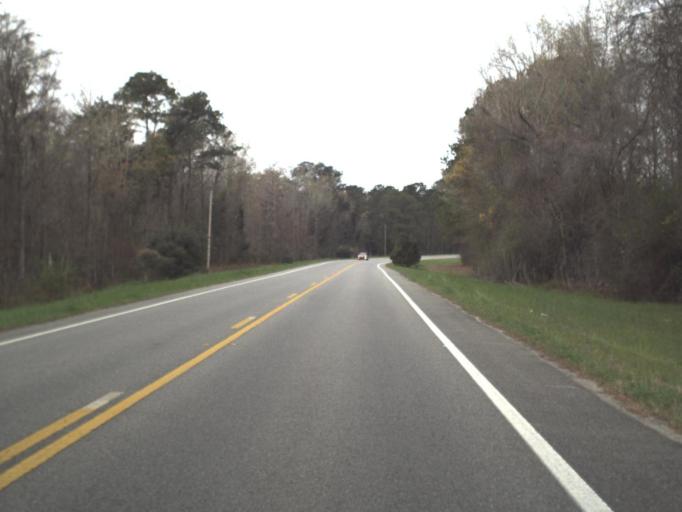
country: US
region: Florida
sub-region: Jefferson County
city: Monticello
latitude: 30.5305
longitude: -83.8233
